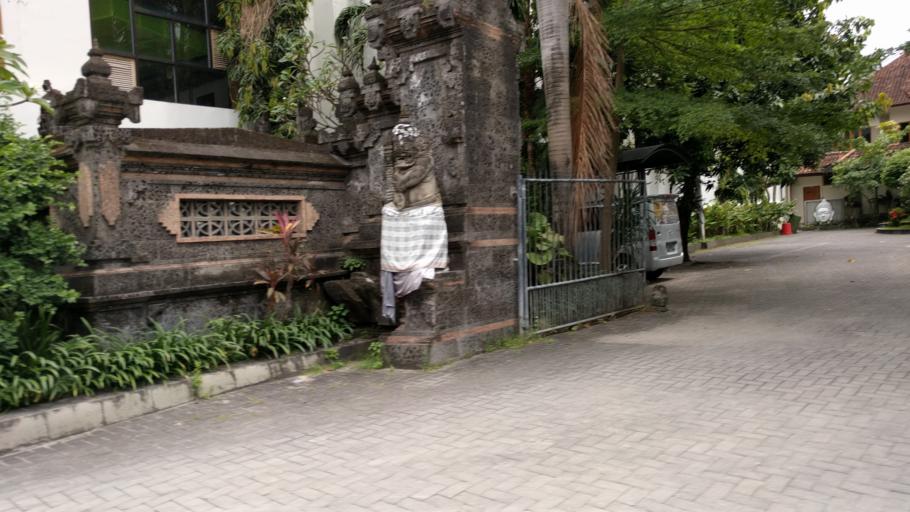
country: ID
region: Bali
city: Kuta
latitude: -8.6745
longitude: 115.1558
